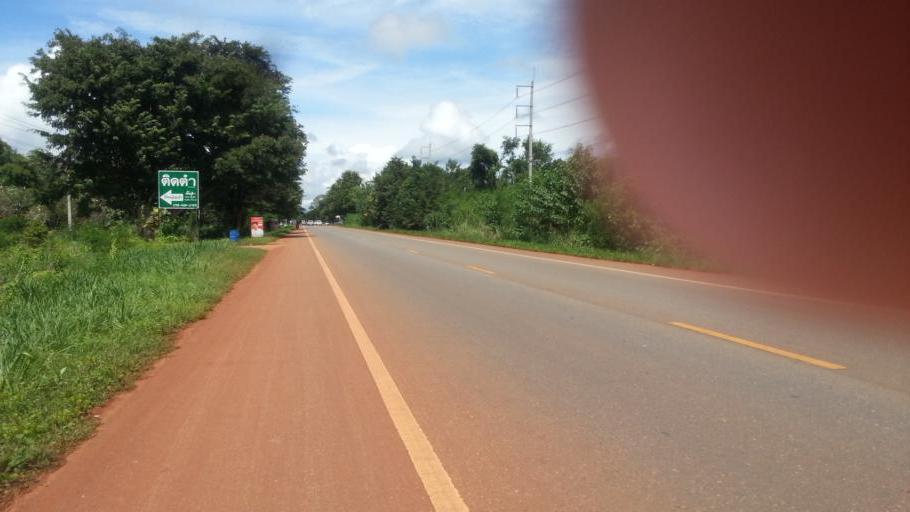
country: TH
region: Kanchanaburi
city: Sai Yok
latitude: 14.1210
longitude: 99.1807
